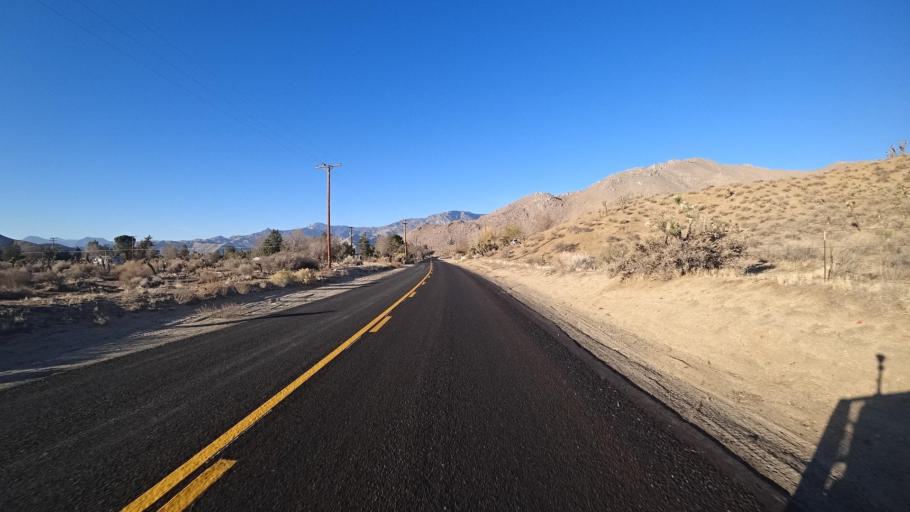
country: US
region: California
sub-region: Kern County
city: Weldon
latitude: 35.6300
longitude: -118.2433
